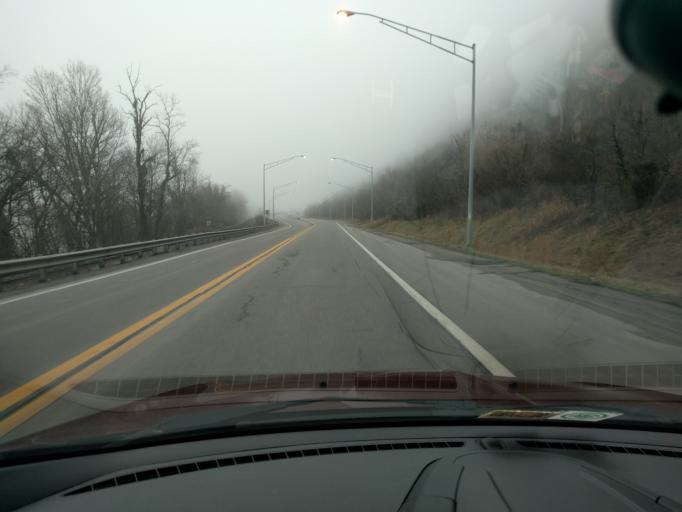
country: US
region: West Virginia
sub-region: Kanawha County
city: Chesapeake
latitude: 38.2029
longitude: -81.4822
